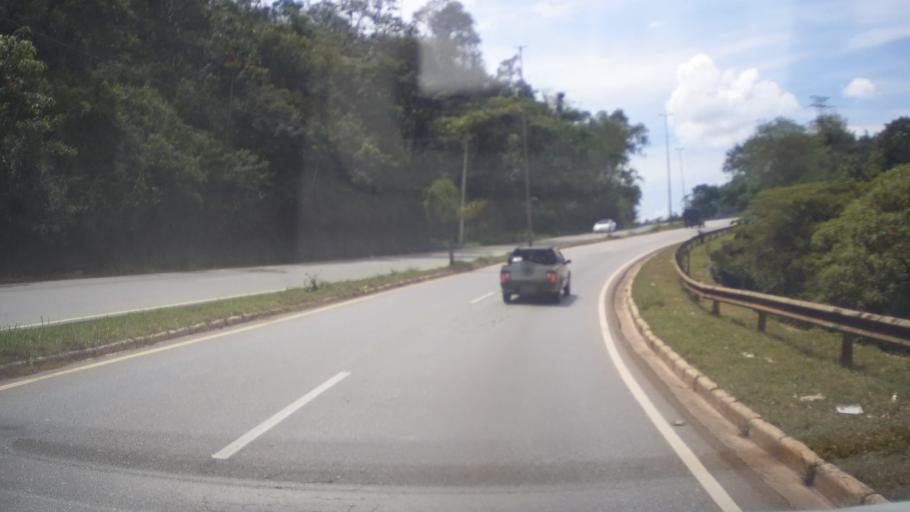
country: BR
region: Minas Gerais
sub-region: Nova Lima
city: Nova Lima
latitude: -19.9959
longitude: -43.9179
